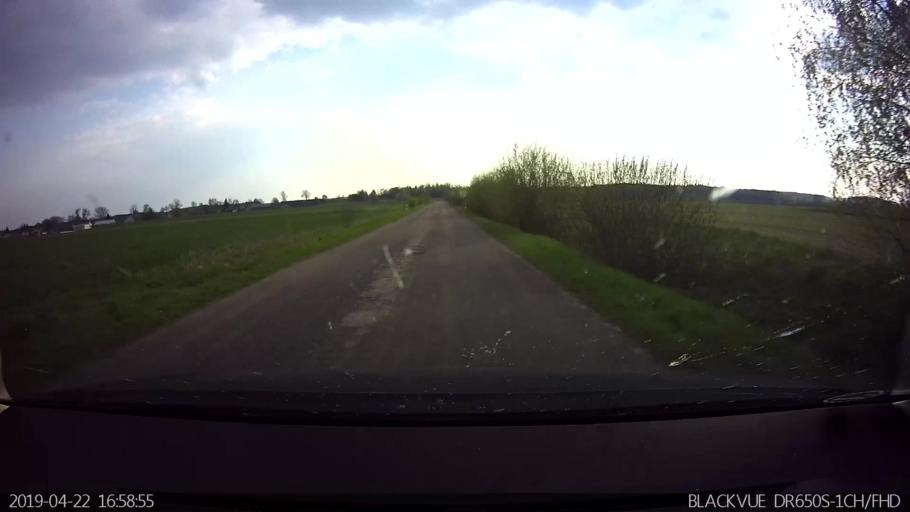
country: PL
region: Podlasie
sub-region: Powiat siemiatycki
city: Drohiczyn
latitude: 52.4666
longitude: 22.7456
